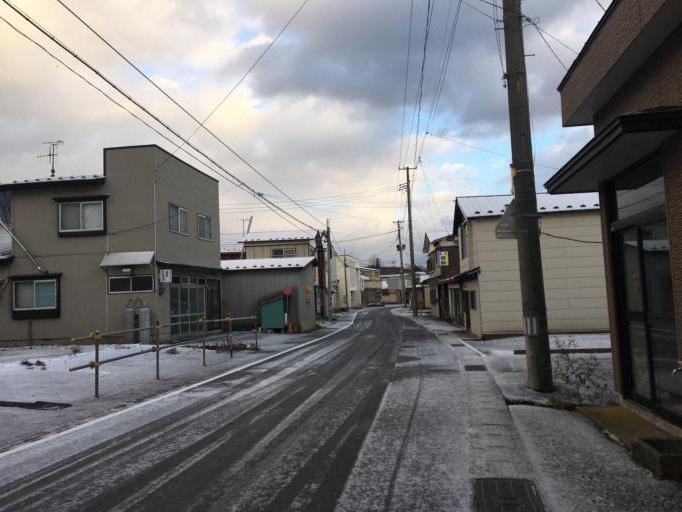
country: JP
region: Aomori
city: Mutsu
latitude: 41.2768
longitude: 141.1565
